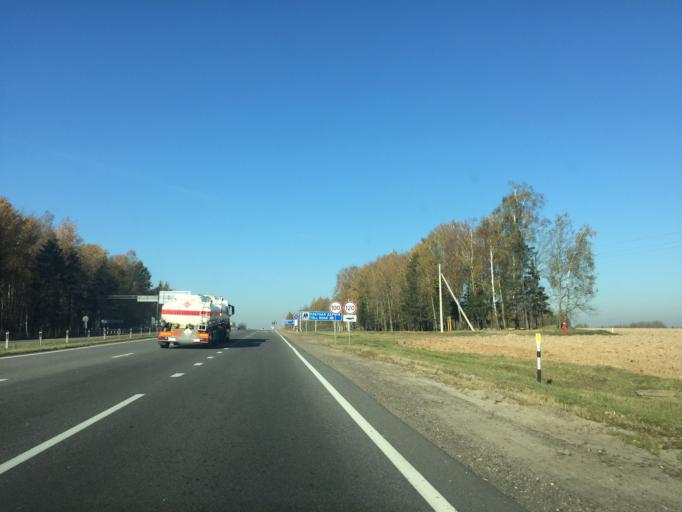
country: BY
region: Mogilev
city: Buynichy
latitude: 53.9506
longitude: 30.2194
